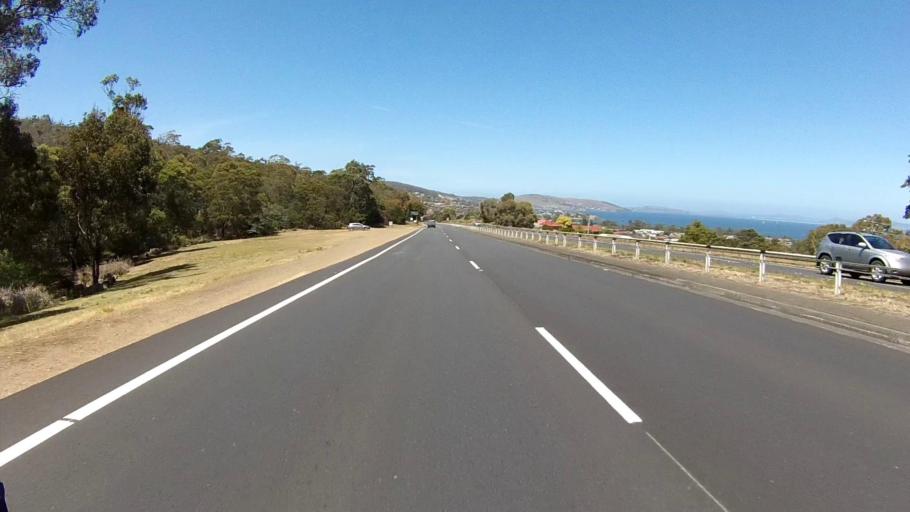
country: AU
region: Tasmania
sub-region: Clarence
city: Howrah
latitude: -42.8698
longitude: 147.3986
